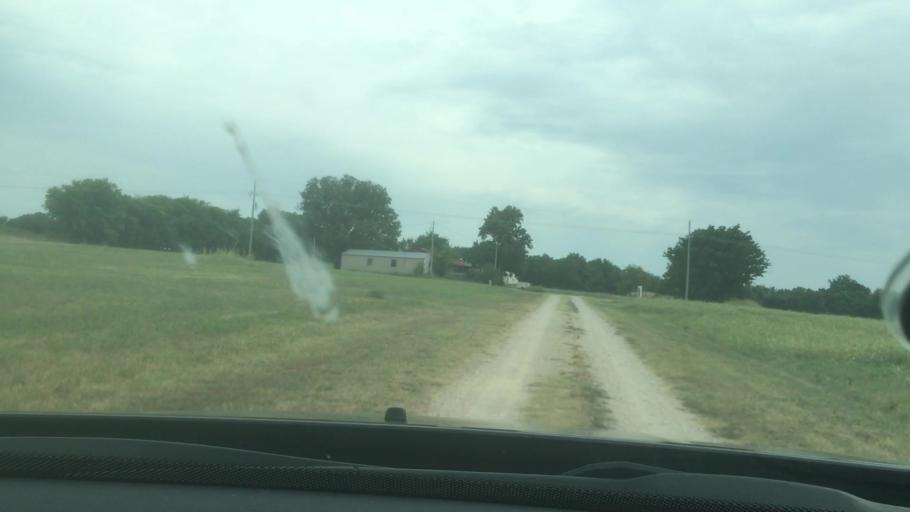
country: US
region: Oklahoma
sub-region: Murray County
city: Davis
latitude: 34.4783
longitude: -97.0587
